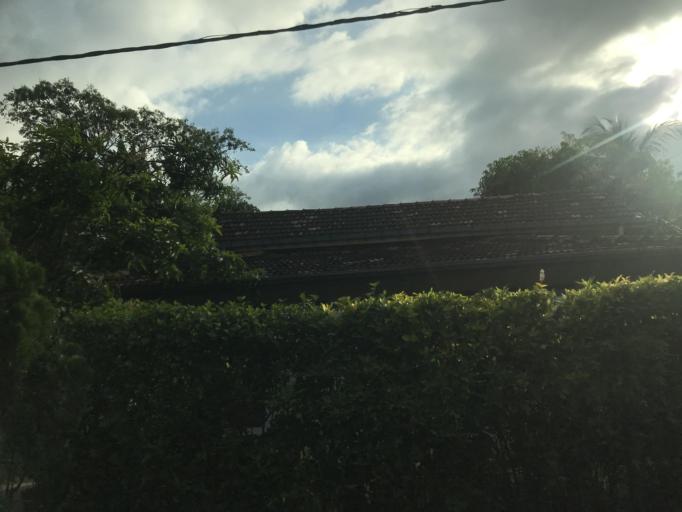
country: LK
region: Western
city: Gampaha
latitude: 7.0740
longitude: 79.9950
